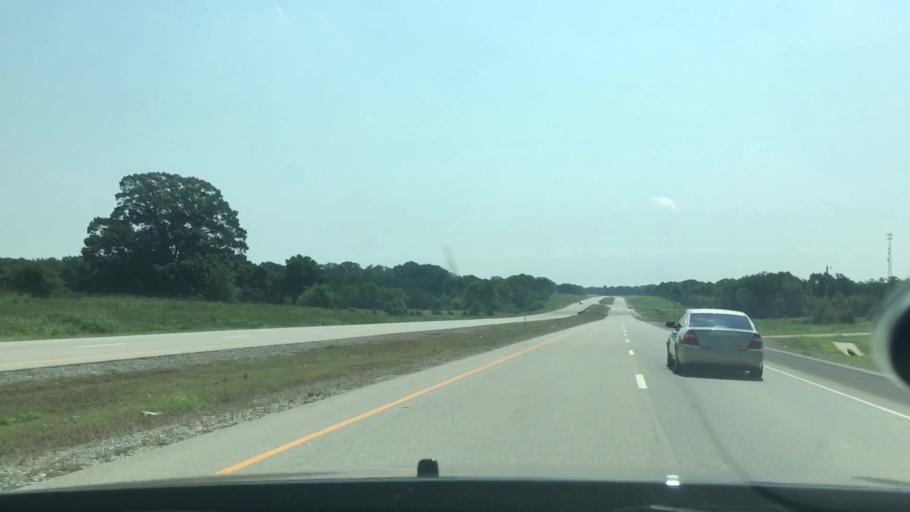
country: US
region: Oklahoma
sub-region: Atoka County
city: Atoka
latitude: 34.3267
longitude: -96.0450
